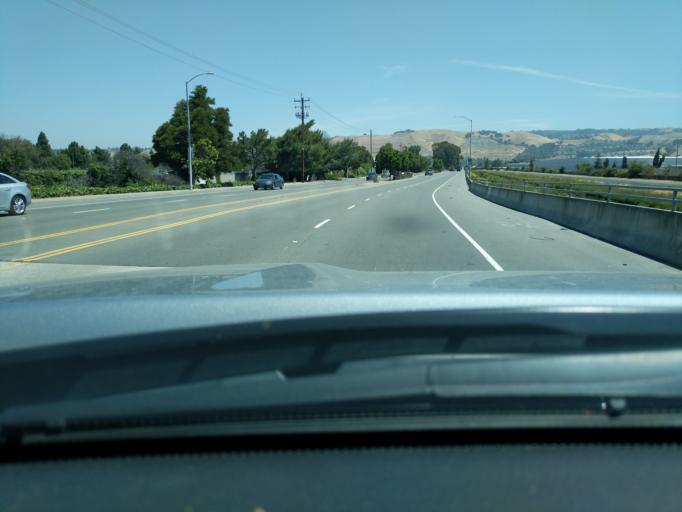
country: US
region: California
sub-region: Alameda County
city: Union City
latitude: 37.6147
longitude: -122.0654
